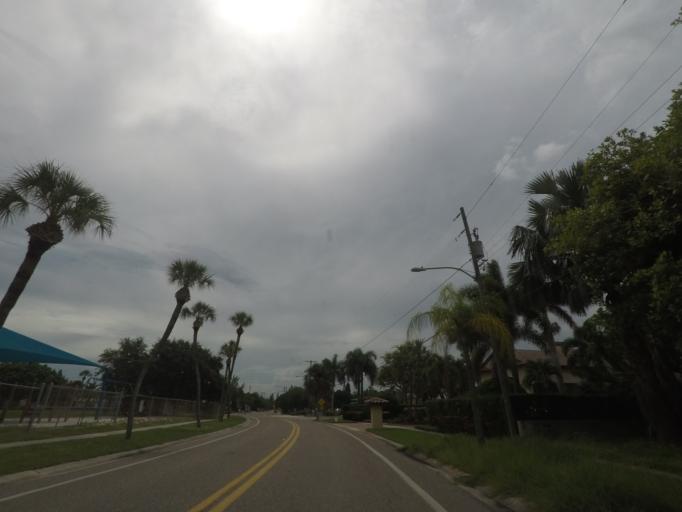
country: US
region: Florida
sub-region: Pinellas County
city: South Pasadena
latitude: 27.7472
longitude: -82.7567
